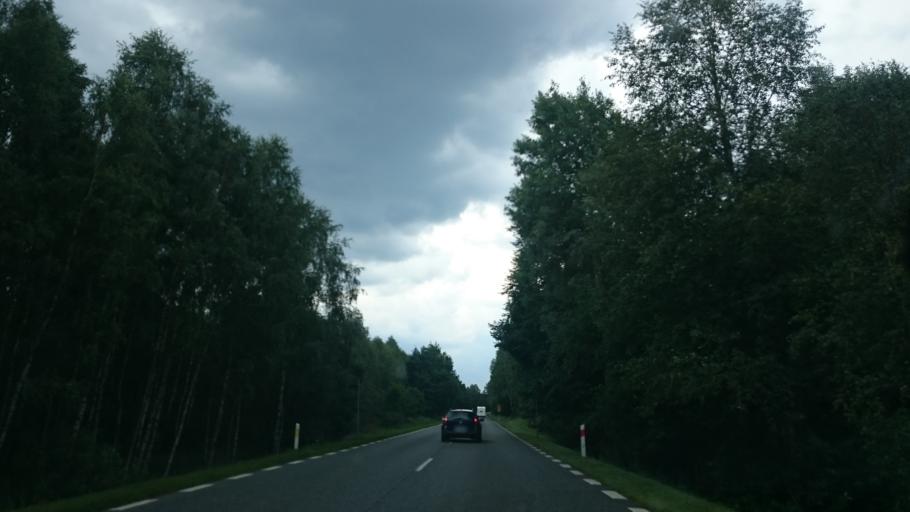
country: PL
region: Kujawsko-Pomorskie
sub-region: Powiat tucholski
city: Lubiewo
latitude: 53.4948
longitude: 18.0750
